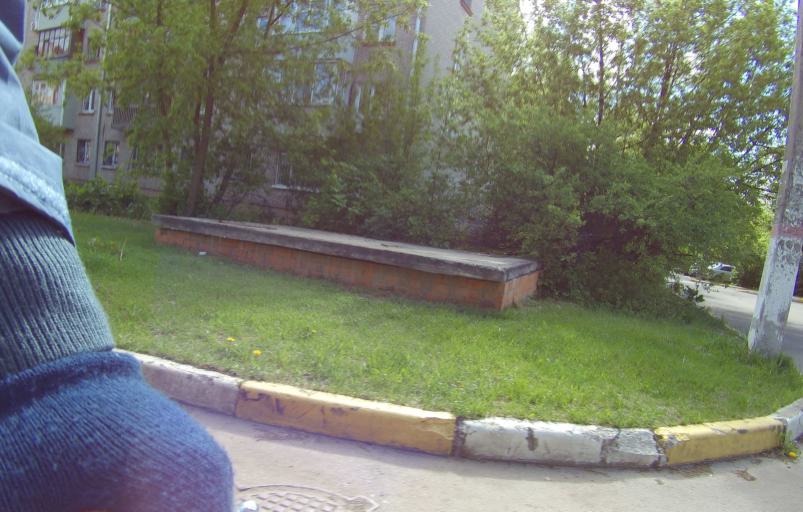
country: RU
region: Moskovskaya
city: Ramenskoye
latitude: 55.5704
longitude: 38.2076
